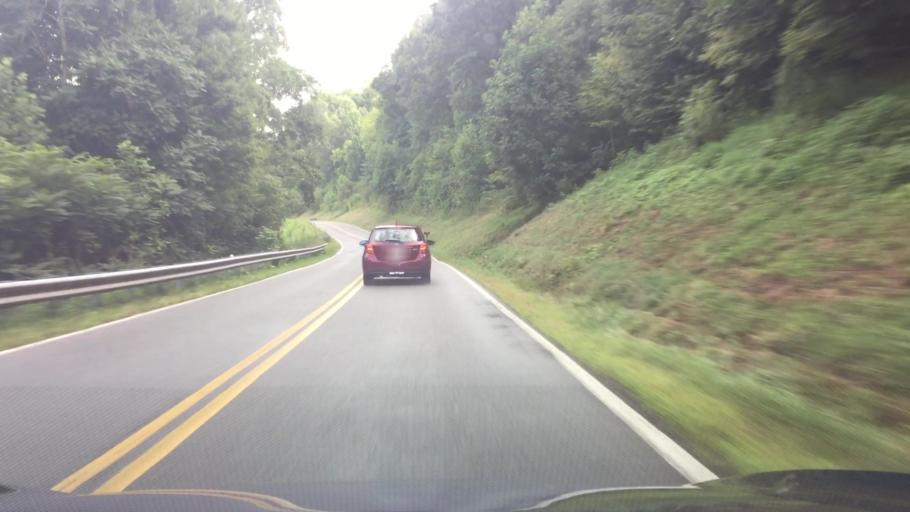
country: US
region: Virginia
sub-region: Smyth County
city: Atkins
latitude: 36.8435
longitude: -81.4244
